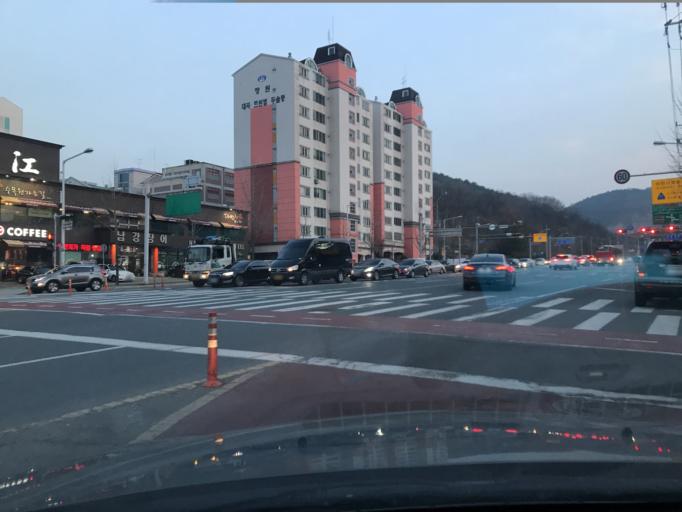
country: KR
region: Daegu
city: Hwawon
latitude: 35.8075
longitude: 128.5204
